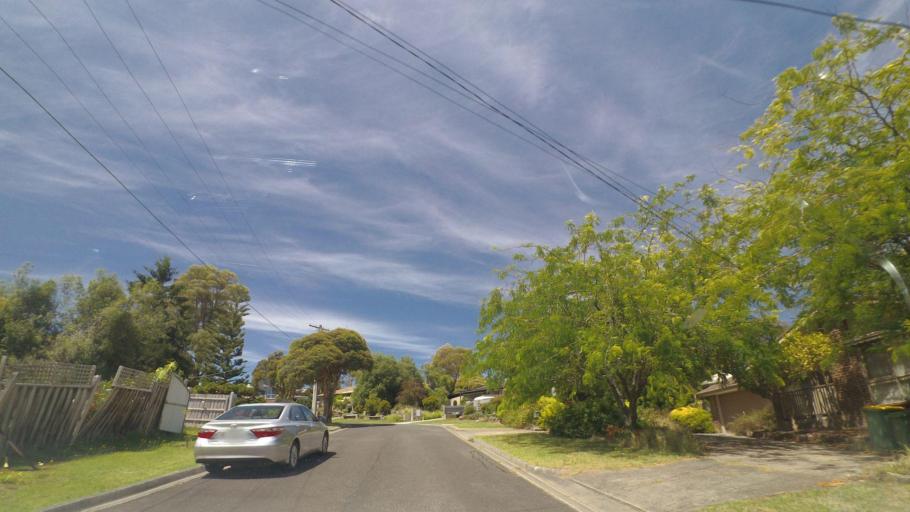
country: AU
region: Victoria
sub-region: Maroondah
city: Croydon North
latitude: -37.7666
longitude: 145.3118
